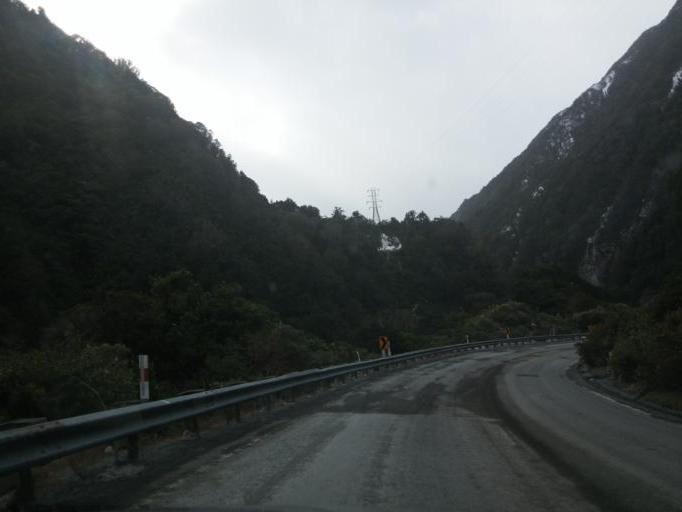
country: NZ
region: West Coast
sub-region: Grey District
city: Greymouth
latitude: -42.8820
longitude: 171.5546
